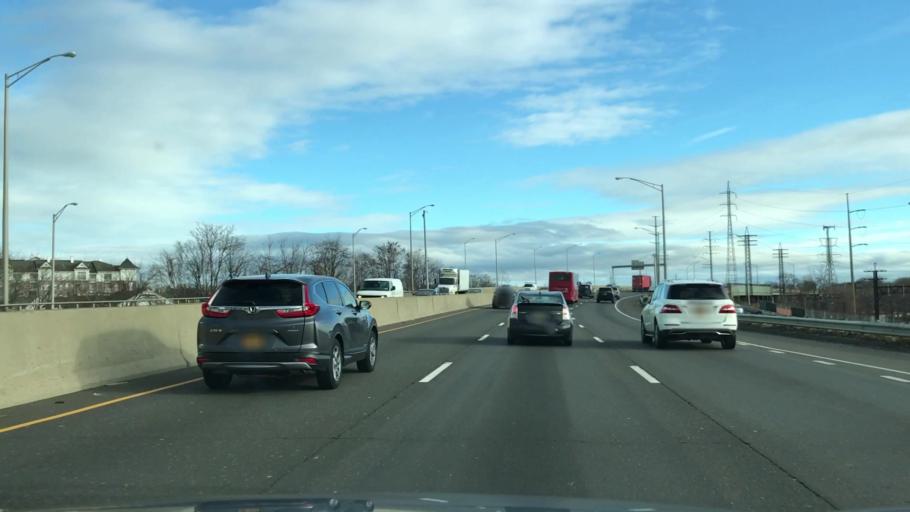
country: US
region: Connecticut
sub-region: Fairfield County
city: Stamford
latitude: 41.0521
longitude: -73.5292
